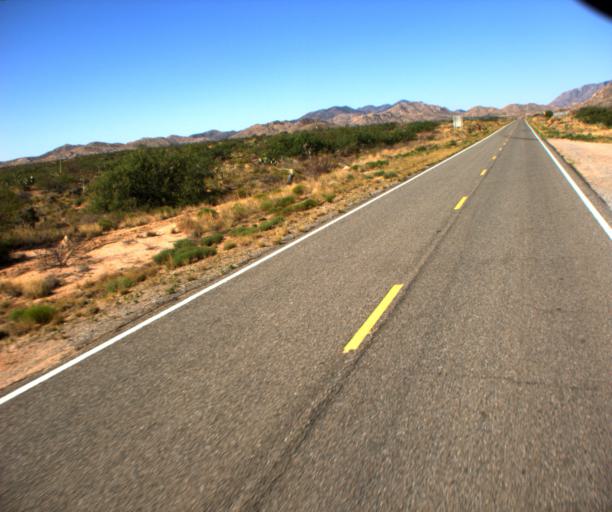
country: US
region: Arizona
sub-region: Graham County
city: Swift Trail Junction
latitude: 32.5935
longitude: -109.6911
